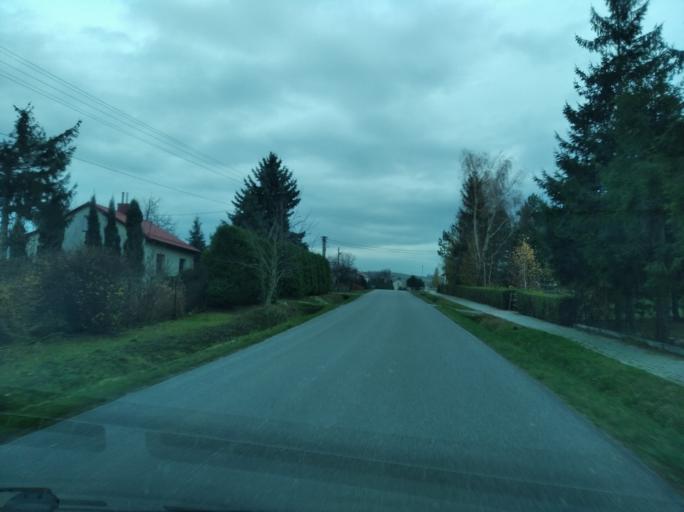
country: PL
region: Subcarpathian Voivodeship
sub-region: Powiat ropczycko-sedziszowski
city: Iwierzyce
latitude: 50.0068
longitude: 21.7555
